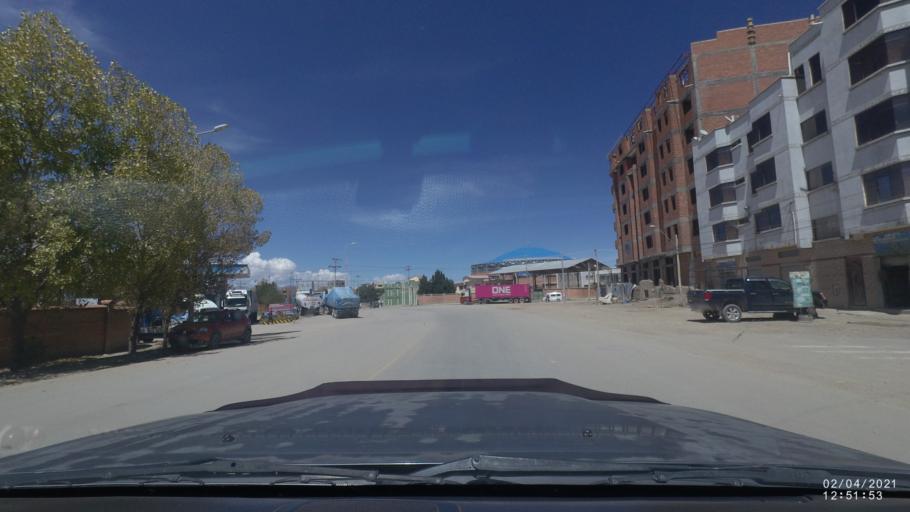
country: BO
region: Oruro
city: Oruro
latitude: -17.9853
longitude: -67.1358
